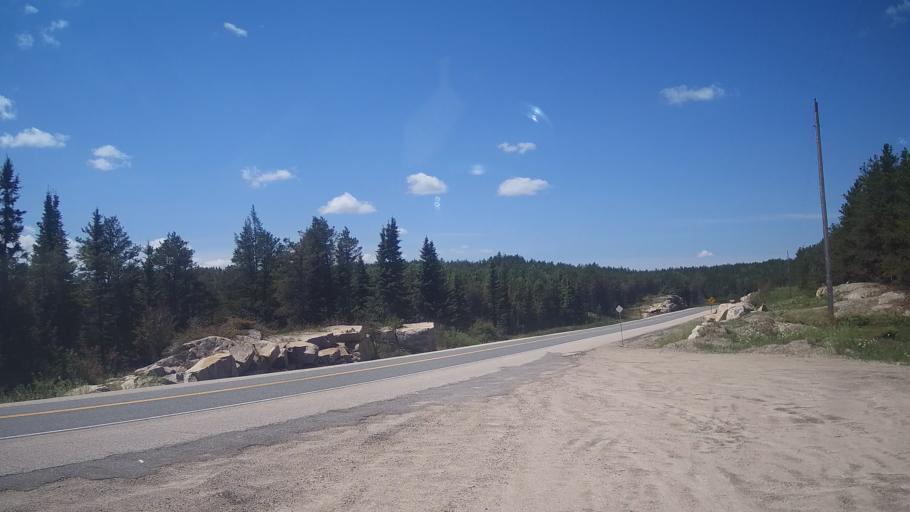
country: CA
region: Ontario
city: Ear Falls
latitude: 49.8411
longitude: -93.8270
